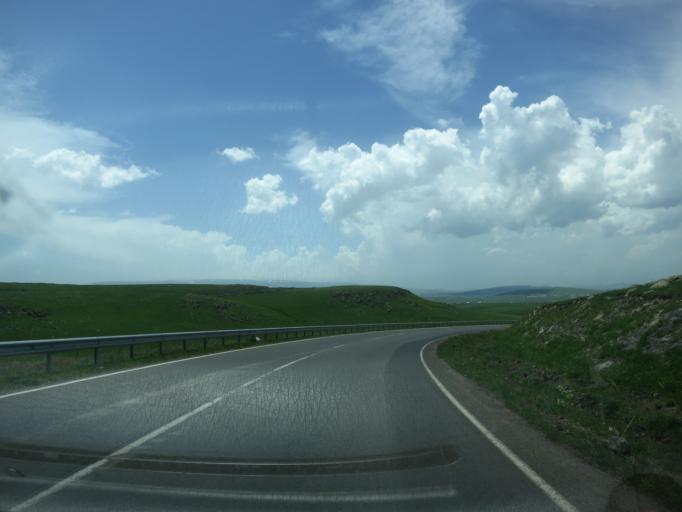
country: GE
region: Samtskhe-Javakheti
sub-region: Ninotsminda
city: Ninotsminda
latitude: 41.2950
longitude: 43.6785
